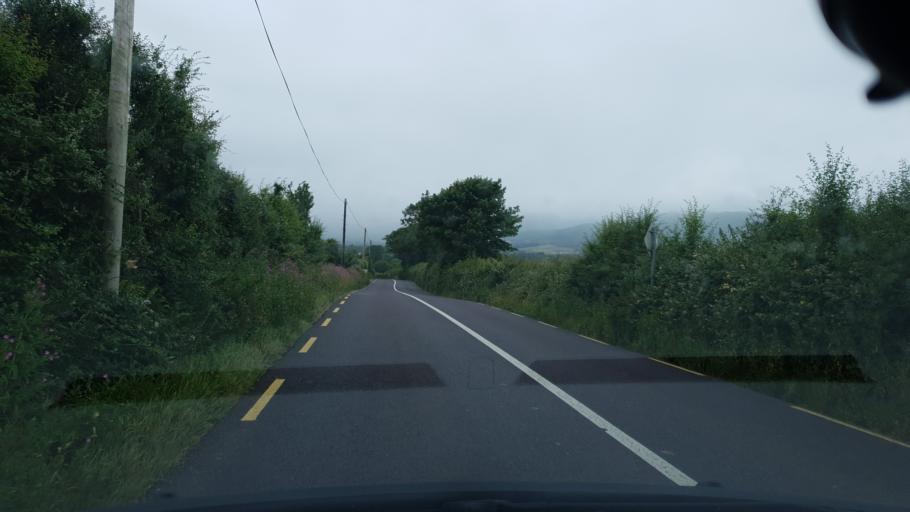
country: IE
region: Munster
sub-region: Ciarrai
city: Tralee
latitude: 52.1625
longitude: -9.6930
